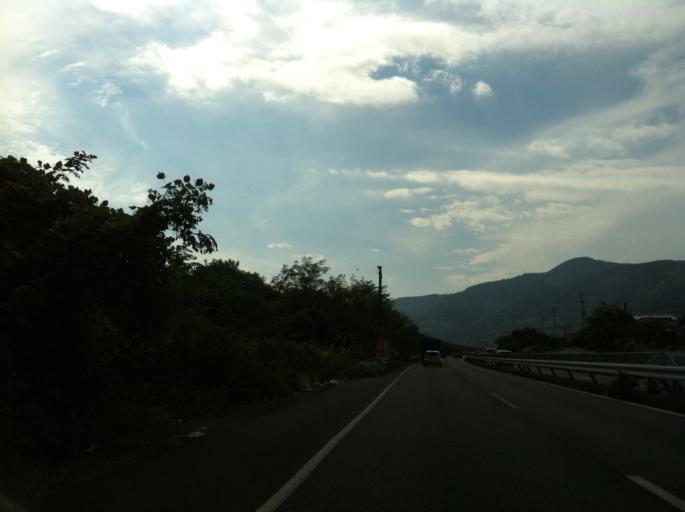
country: JP
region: Shizuoka
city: Fujinomiya
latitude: 35.1087
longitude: 138.5710
